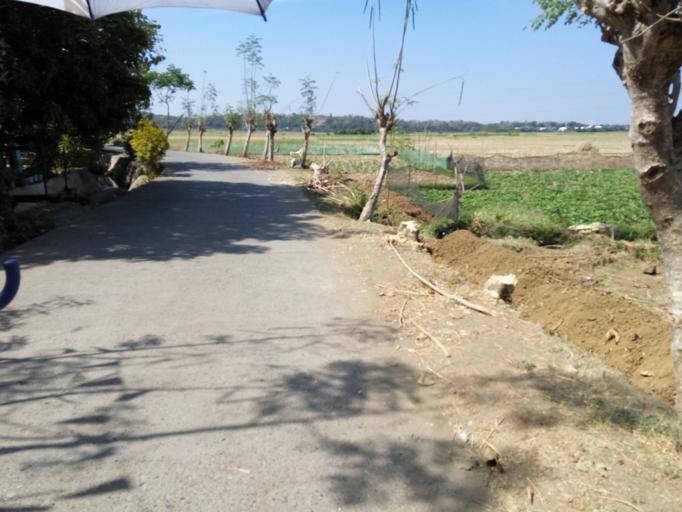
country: PH
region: Ilocos
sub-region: Province of Ilocos Sur
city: Santa Maria
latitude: 16.9440
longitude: 120.4600
